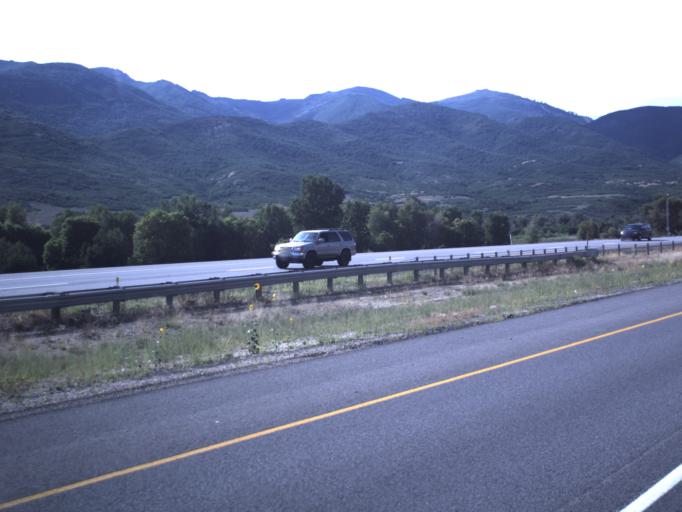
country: US
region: Utah
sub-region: Wasatch County
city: Heber
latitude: 40.5622
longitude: -111.4277
